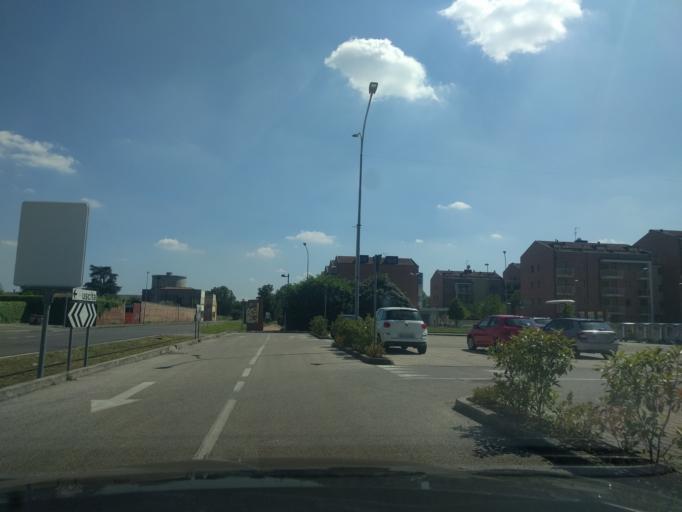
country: IT
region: Emilia-Romagna
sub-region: Provincia di Ferrara
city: Ferrara
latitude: 44.8460
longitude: 11.5986
